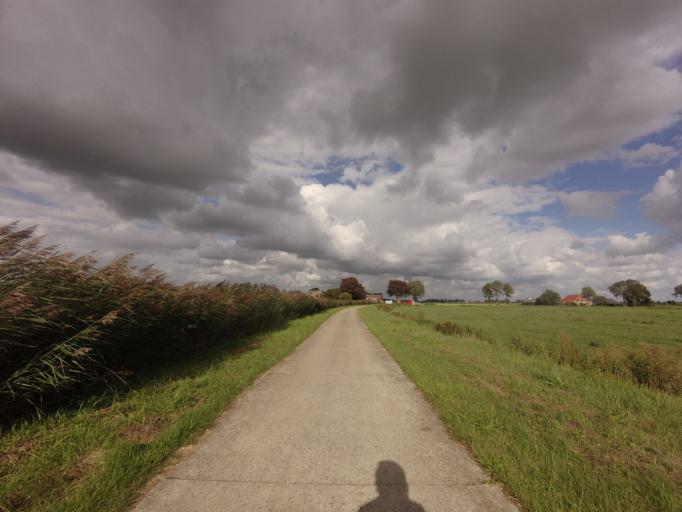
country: NL
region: Overijssel
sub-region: Gemeente Steenwijkerland
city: Blokzijl
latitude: 52.7400
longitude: 6.0021
